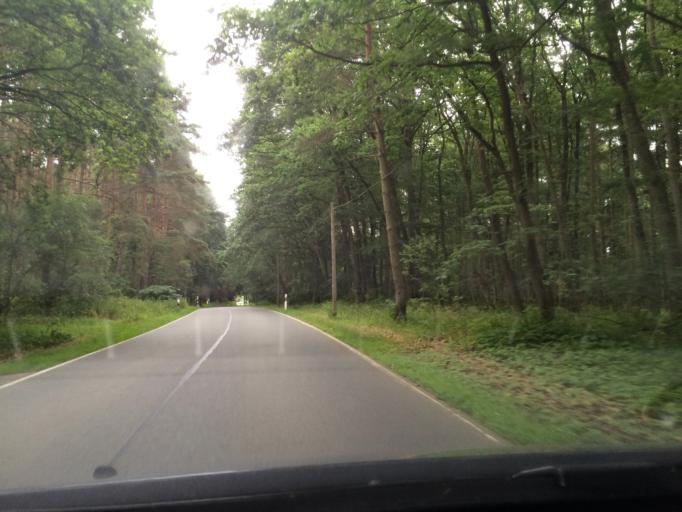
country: DE
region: Mecklenburg-Vorpommern
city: Prohn
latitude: 54.4282
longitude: 13.0258
